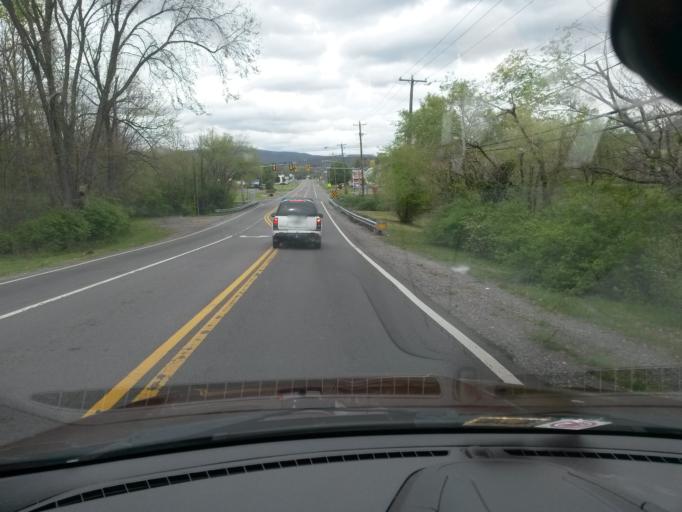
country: US
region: Virginia
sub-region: Roanoke County
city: Hollins
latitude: 37.3332
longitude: -79.9545
